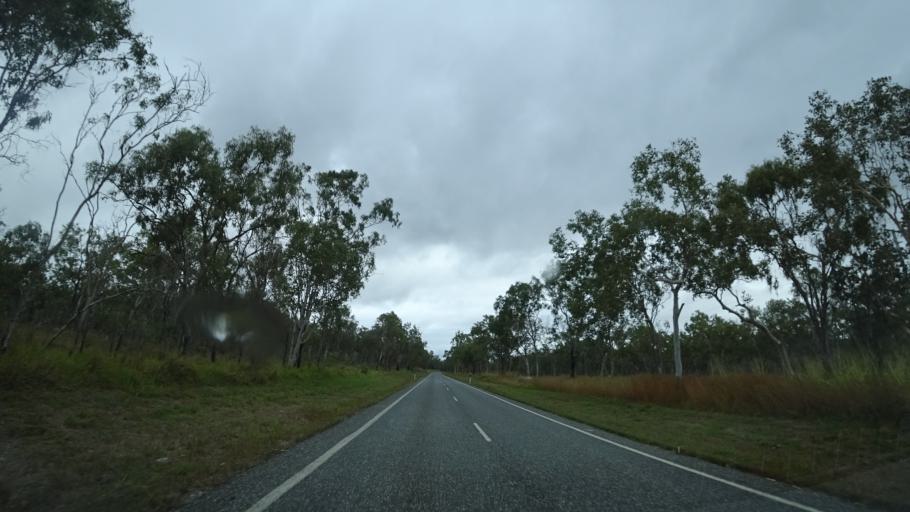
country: AU
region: Queensland
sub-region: Cairns
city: Port Douglas
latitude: -16.7245
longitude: 145.3530
